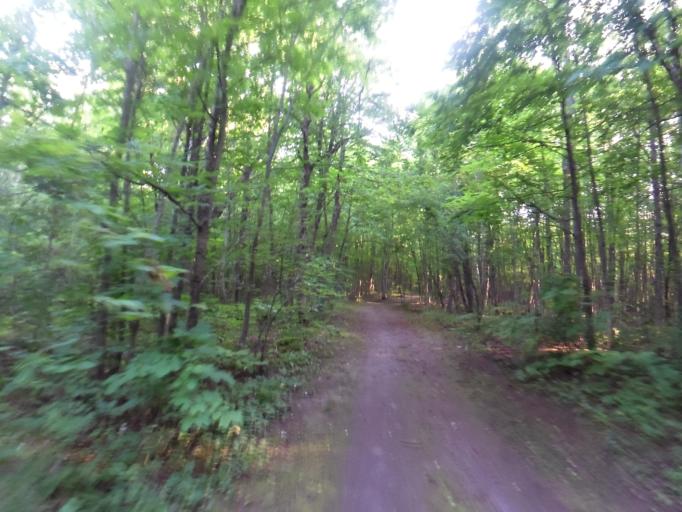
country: CA
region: Ontario
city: Bells Corners
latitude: 45.3089
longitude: -75.8169
